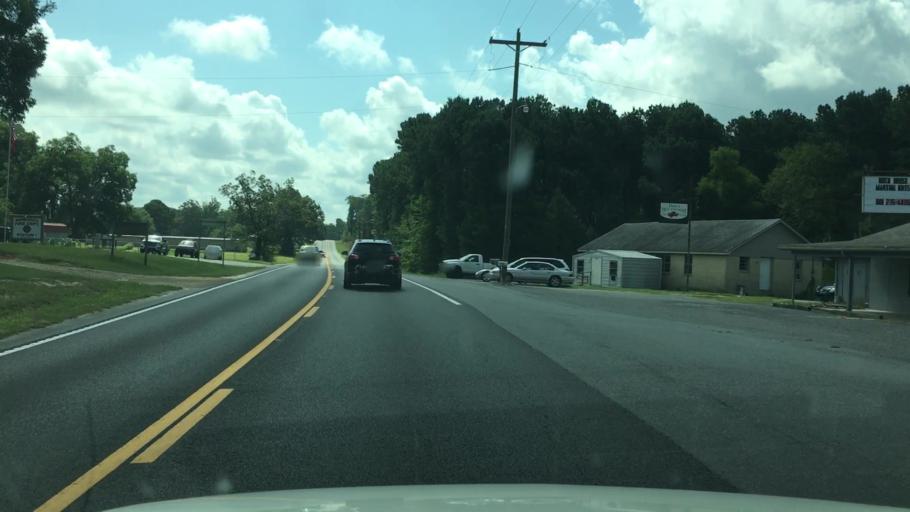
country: US
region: Arkansas
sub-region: Garland County
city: Lake Hamilton
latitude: 34.2684
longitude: -93.1437
